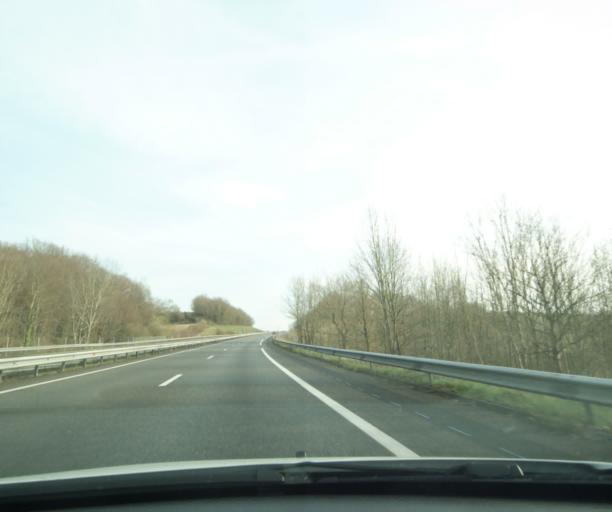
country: FR
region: Midi-Pyrenees
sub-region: Departement des Hautes-Pyrenees
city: Barbazan-Debat
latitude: 43.2054
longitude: 0.1453
